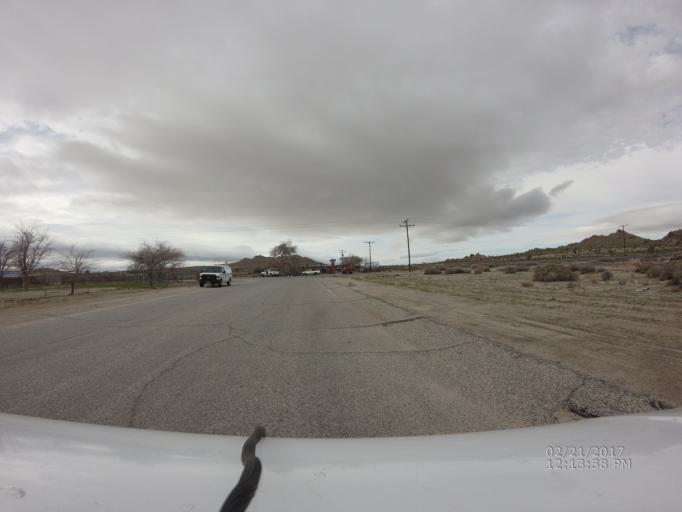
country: US
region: California
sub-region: Los Angeles County
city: Lake Los Angeles
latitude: 34.6349
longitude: -117.8622
